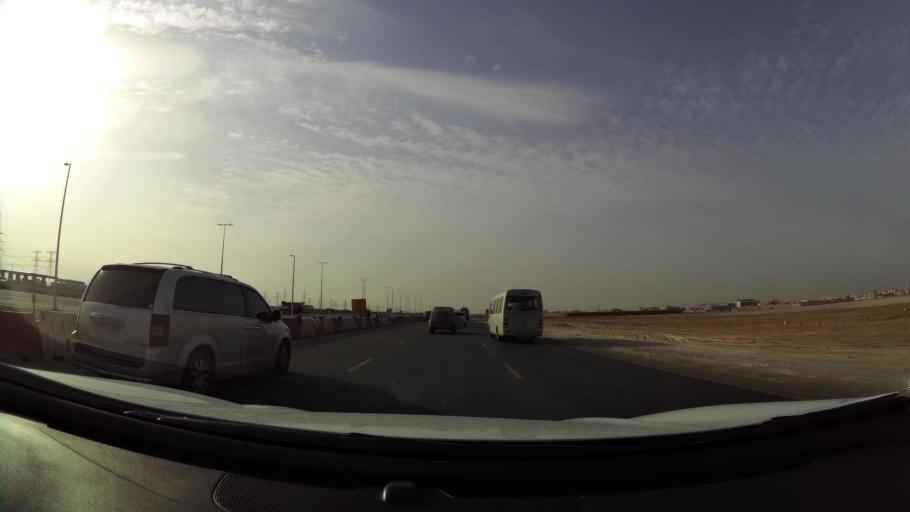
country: AE
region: Abu Dhabi
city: Abu Dhabi
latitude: 24.2973
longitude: 54.5430
